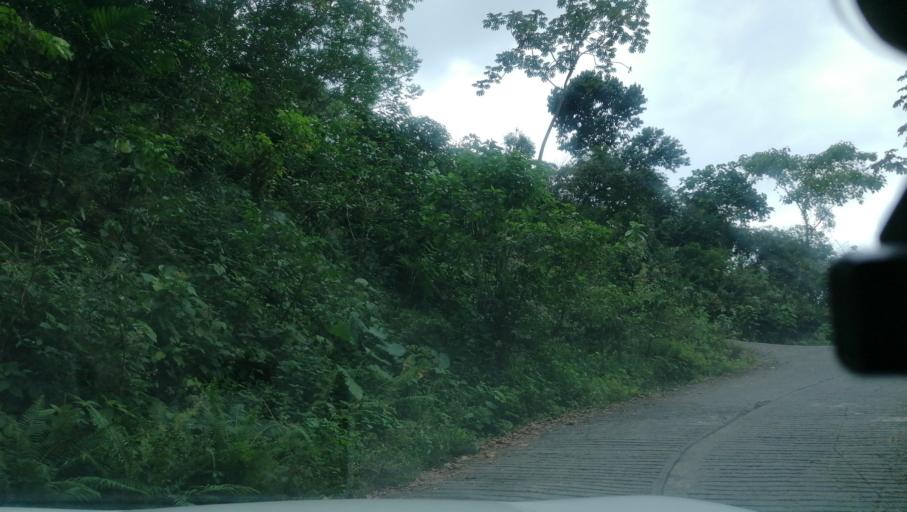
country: MX
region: Chiapas
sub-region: Cacahoatan
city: Benito Juarez
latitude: 15.0995
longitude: -92.1880
